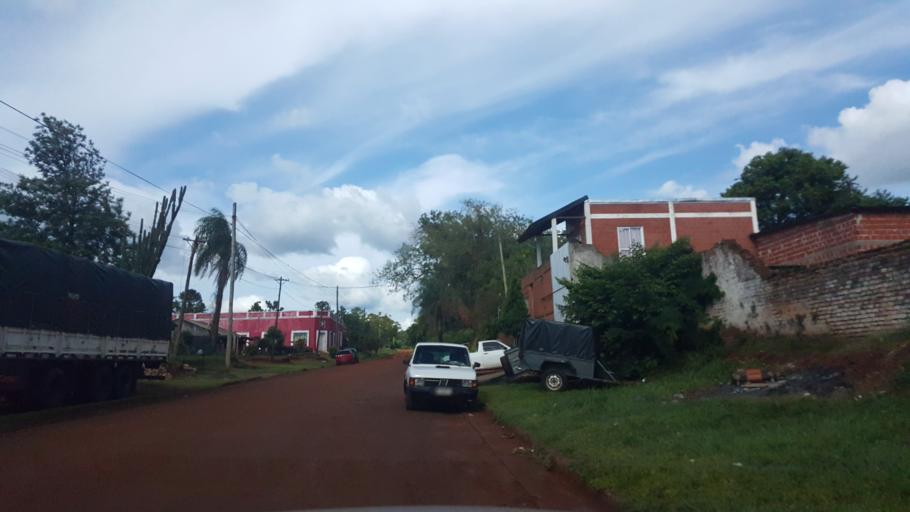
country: AR
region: Misiones
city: Santa Ana
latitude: -27.3709
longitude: -55.5800
